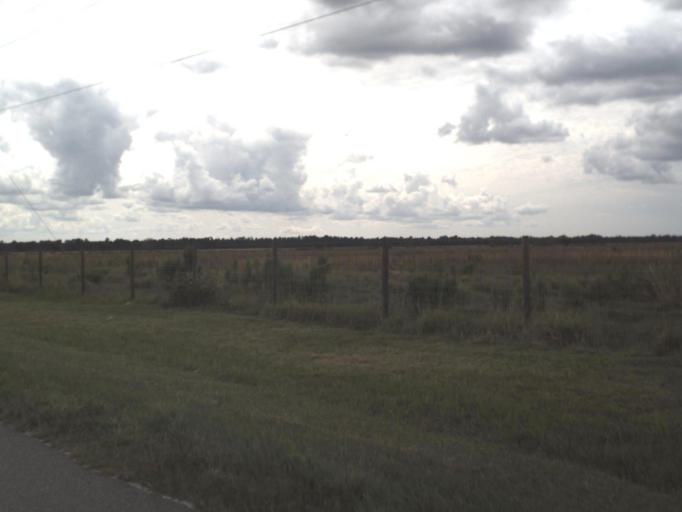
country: US
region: Florida
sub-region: DeSoto County
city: Nocatee
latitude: 26.9857
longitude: -81.7606
